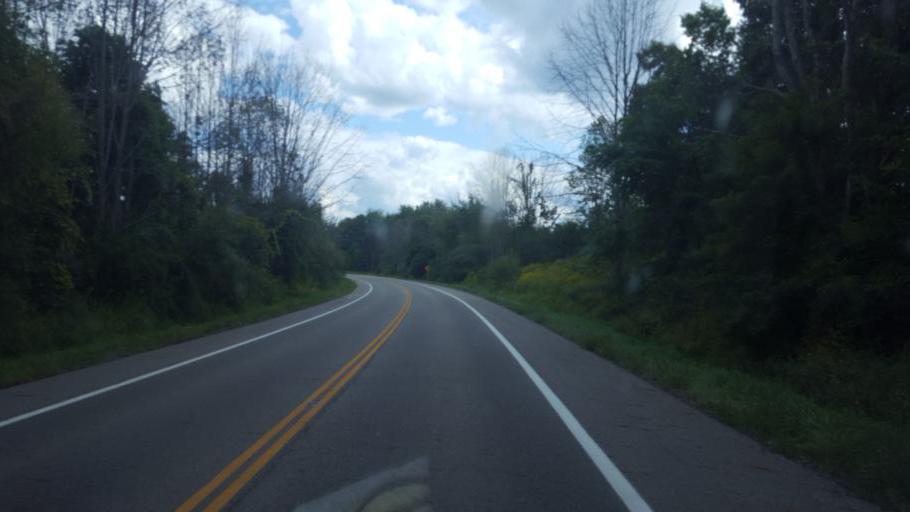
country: US
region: Ohio
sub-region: Portage County
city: Hiram
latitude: 41.2973
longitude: -81.1427
